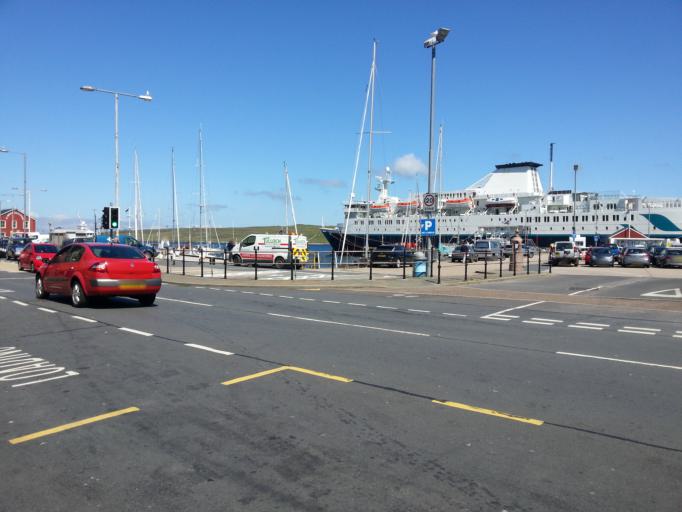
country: GB
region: Scotland
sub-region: Shetland Islands
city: Shetland
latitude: 60.1537
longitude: -1.1427
